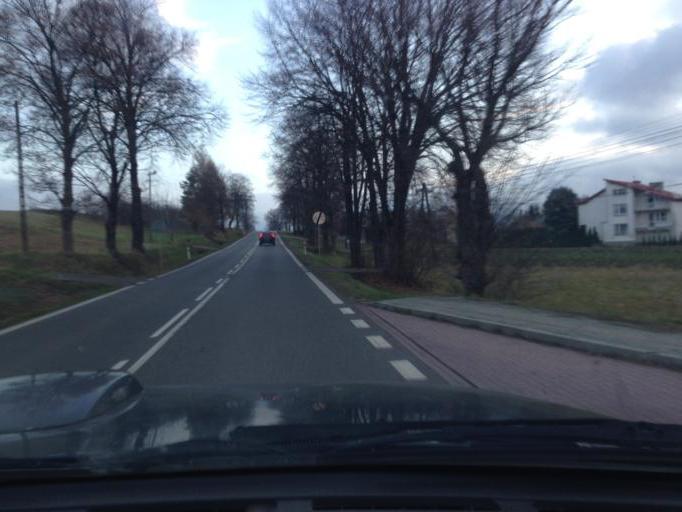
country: PL
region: Subcarpathian Voivodeship
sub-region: Powiat jasielski
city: Nowy Zmigrod
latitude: 49.6315
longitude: 21.5292
